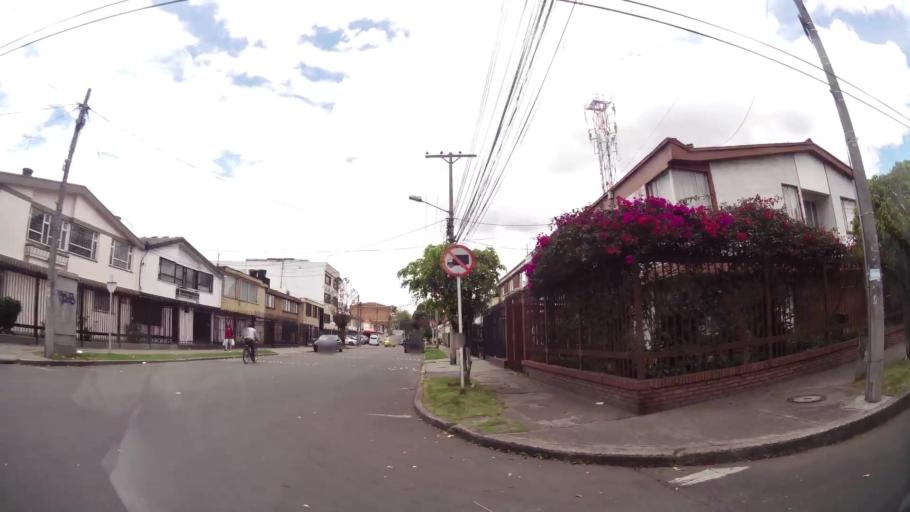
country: CO
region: Bogota D.C.
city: Bogota
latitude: 4.6719
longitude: -74.1044
